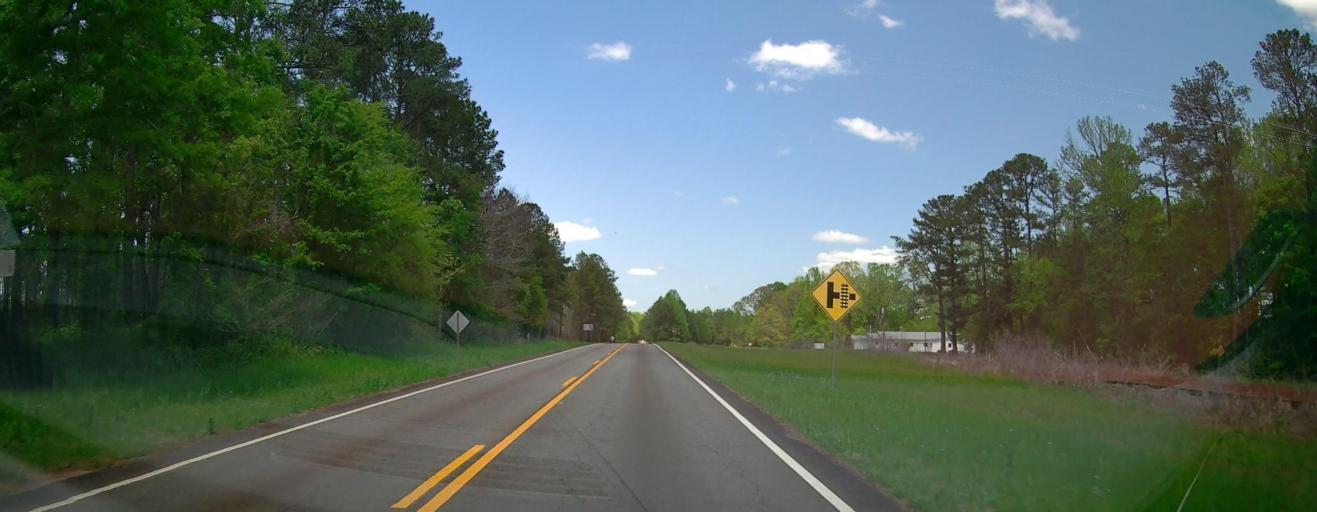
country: US
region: Georgia
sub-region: Jones County
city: Gray
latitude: 33.1204
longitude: -83.6256
